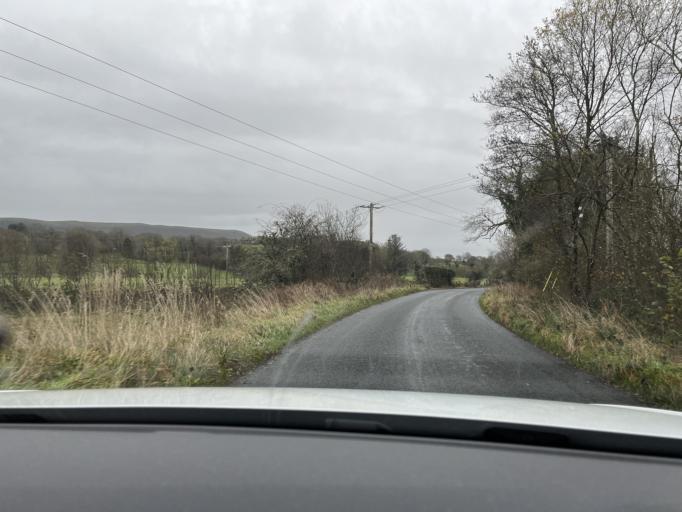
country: IE
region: Connaught
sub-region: County Leitrim
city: Manorhamilton
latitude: 54.2961
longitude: -8.1987
